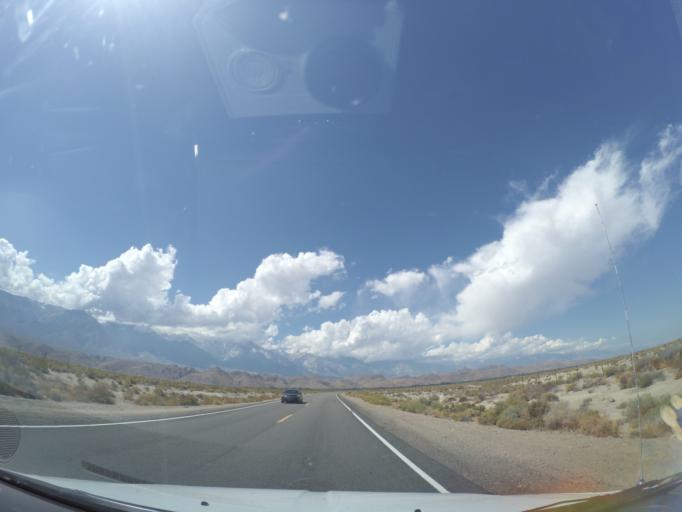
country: US
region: California
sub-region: Inyo County
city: Lone Pine
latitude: 36.5763
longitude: -118.0248
